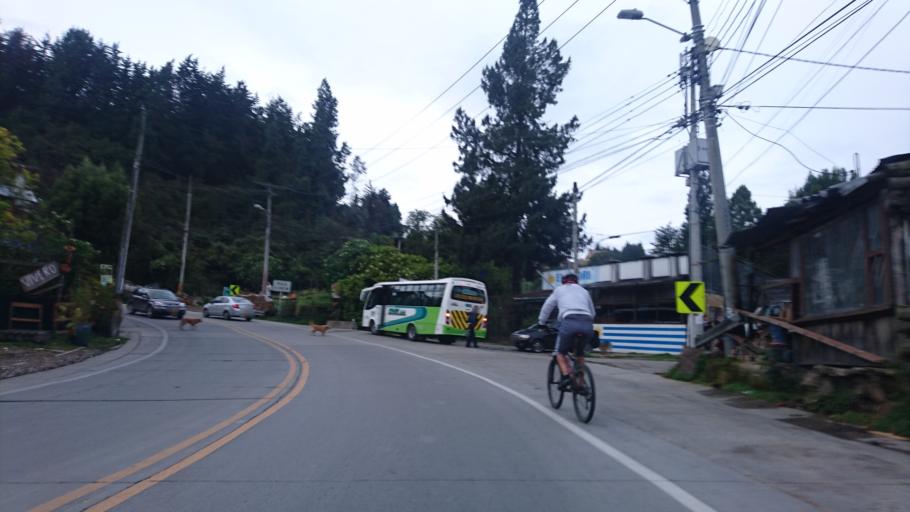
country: CO
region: Bogota D.C.
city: Barrio San Luis
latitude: 4.6665
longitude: -74.0141
